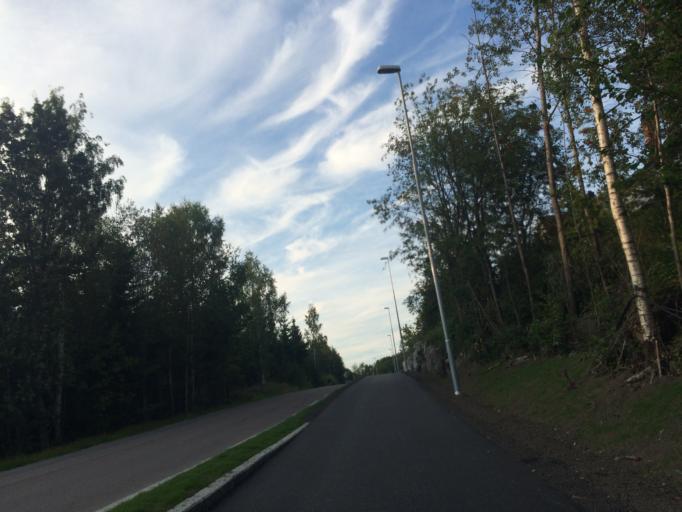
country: NO
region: Akershus
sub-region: Ski
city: Ski
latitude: 59.7036
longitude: 10.8445
